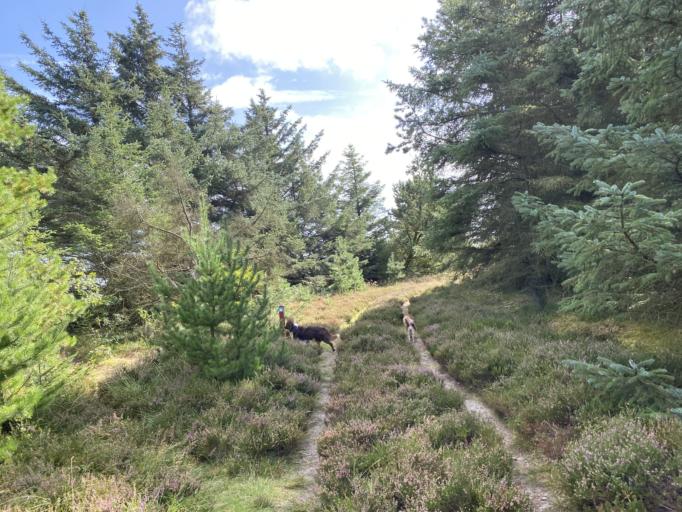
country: DK
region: Central Jutland
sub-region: Holstebro Kommune
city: Ulfborg
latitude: 56.3153
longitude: 8.1374
